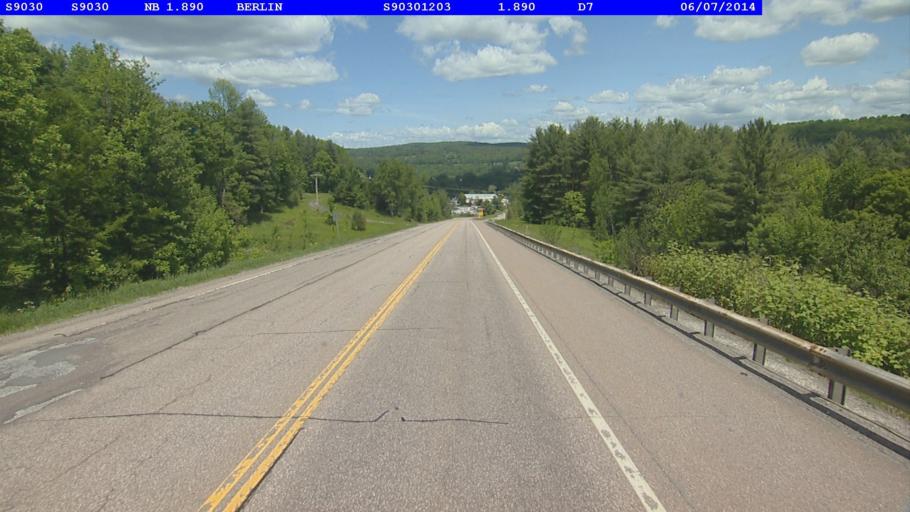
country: US
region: Vermont
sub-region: Washington County
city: Montpelier
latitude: 44.2272
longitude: -72.5572
